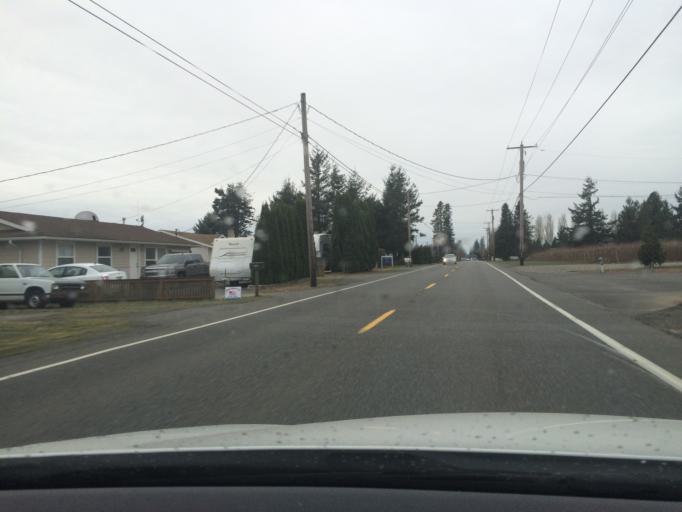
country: US
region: Washington
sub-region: Whatcom County
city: Lynden
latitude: 48.8917
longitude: -122.4655
